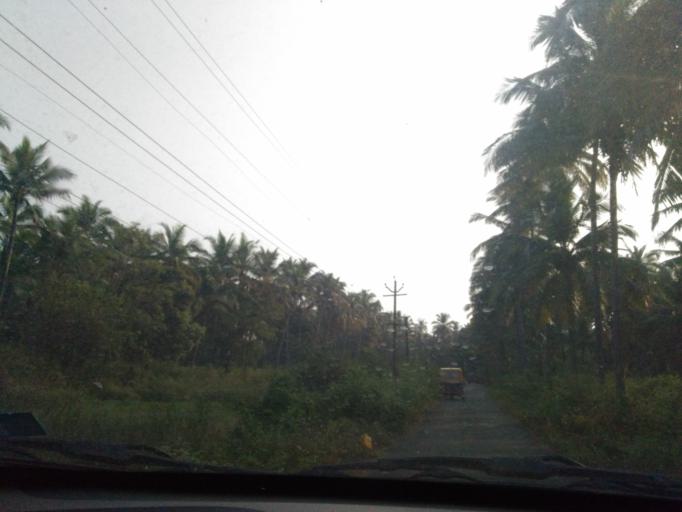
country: IN
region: Goa
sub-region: South Goa
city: Cuncolim
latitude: 15.1748
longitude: 73.9737
